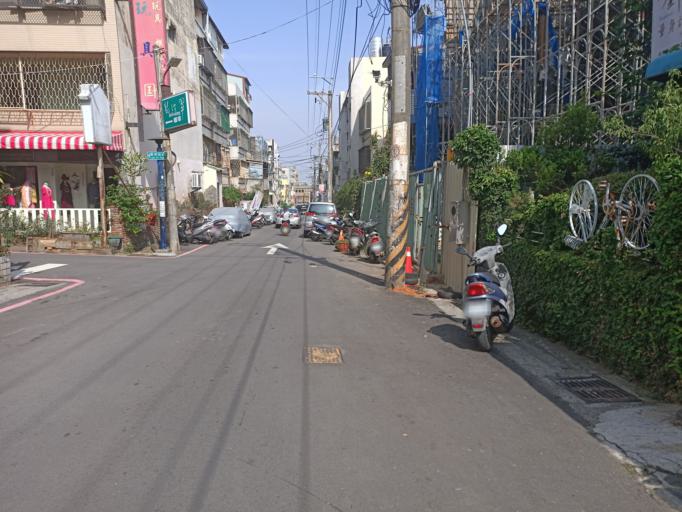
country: TW
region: Taiwan
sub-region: Taichung City
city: Taichung
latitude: 24.1874
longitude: 120.5931
